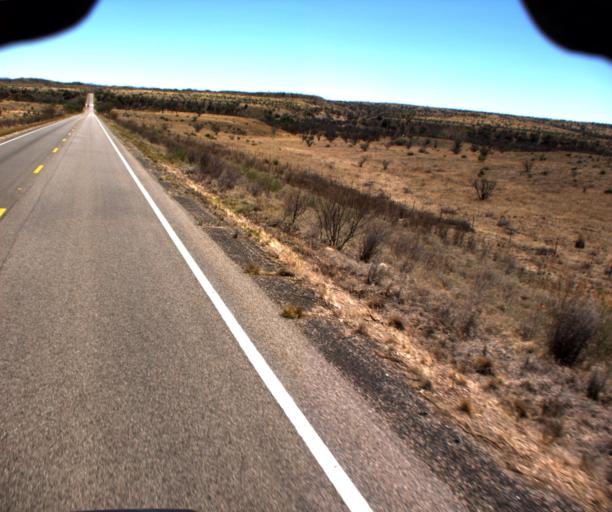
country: US
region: Arizona
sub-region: Pima County
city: Corona de Tucson
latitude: 31.7431
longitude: -110.6669
